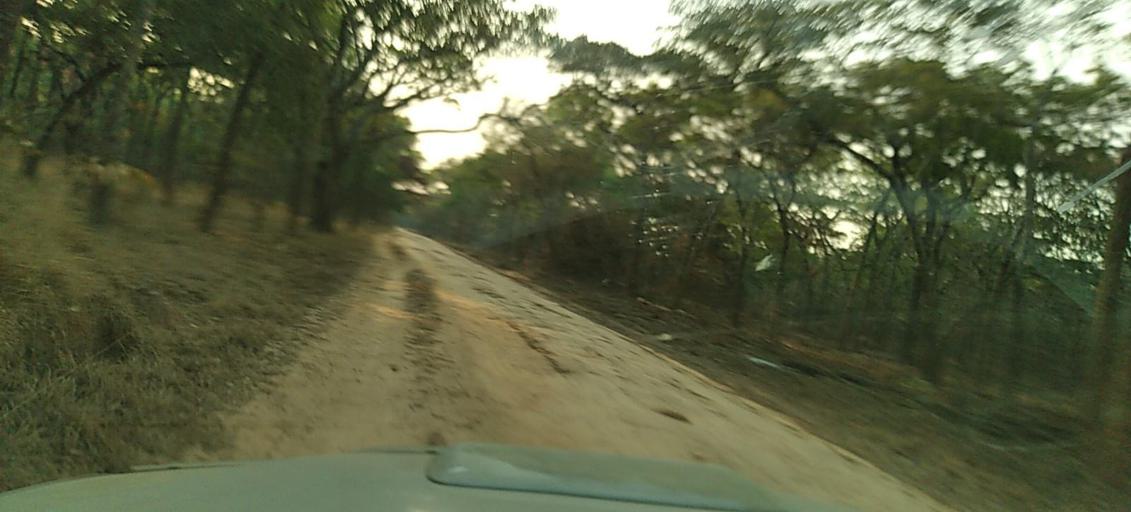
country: ZM
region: North-Western
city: Kasempa
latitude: -13.1567
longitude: 26.4466
